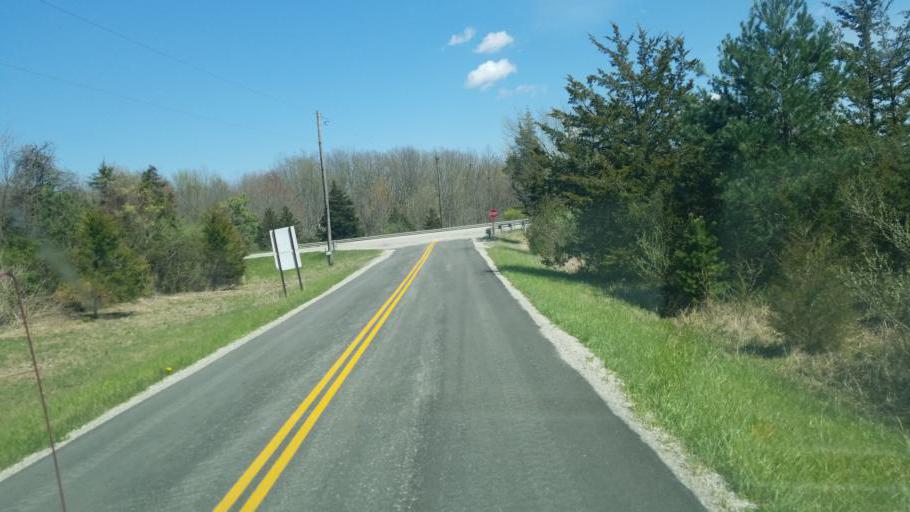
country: US
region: Ohio
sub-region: Delaware County
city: Delaware
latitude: 40.3729
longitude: -83.0748
